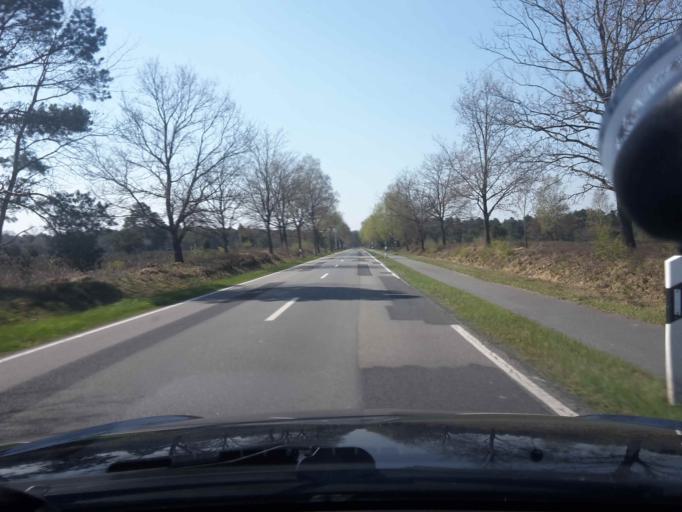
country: DE
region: Lower Saxony
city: Handeloh
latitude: 53.2445
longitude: 9.8706
